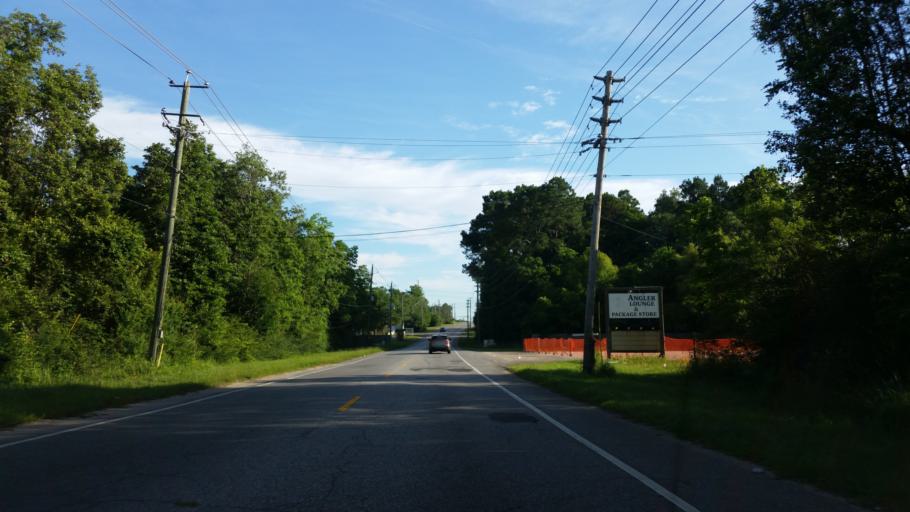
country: US
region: Florida
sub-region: Escambia County
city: Myrtle Grove
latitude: 30.4337
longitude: -87.3083
